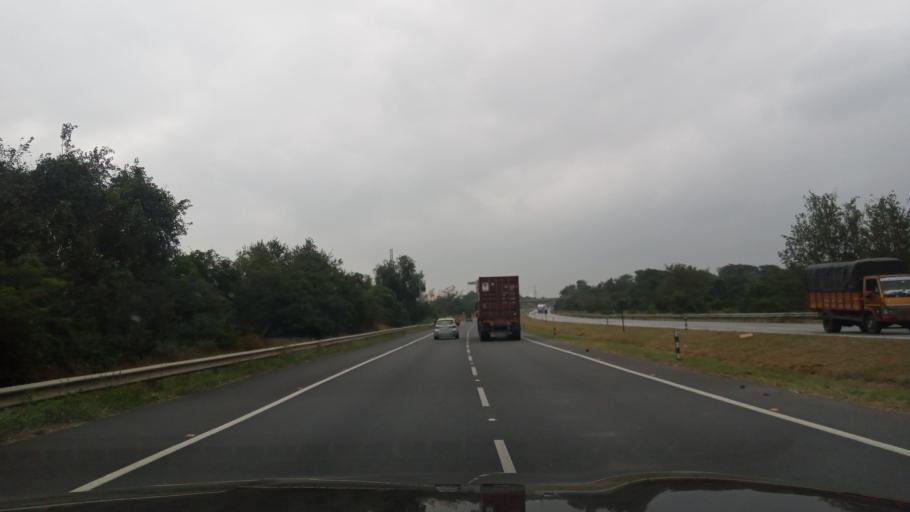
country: IN
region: Karnataka
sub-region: Bangalore Rural
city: Nelamangala
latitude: 13.0174
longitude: 77.4762
